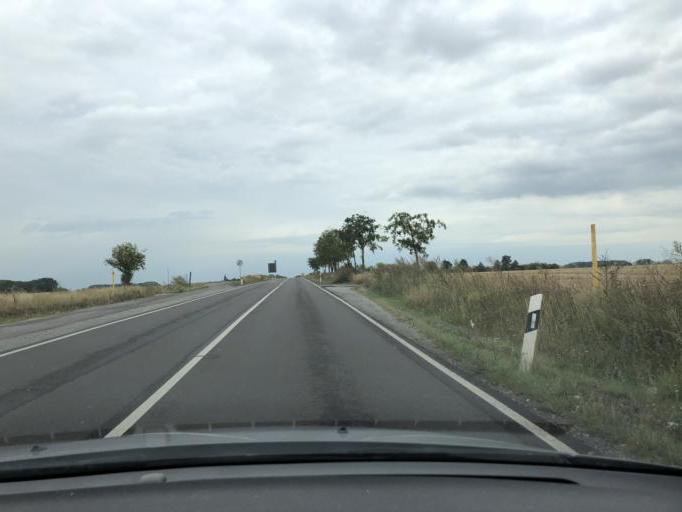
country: DE
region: Saxony-Anhalt
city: Glothe
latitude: 51.8960
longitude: 11.6927
